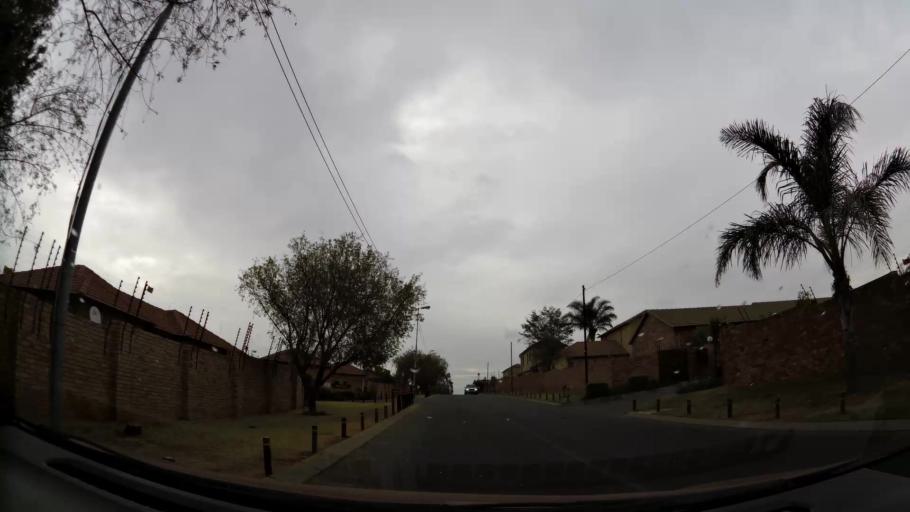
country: ZA
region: Gauteng
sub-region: City of Johannesburg Metropolitan Municipality
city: Roodepoort
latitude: -26.1082
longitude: 27.9038
